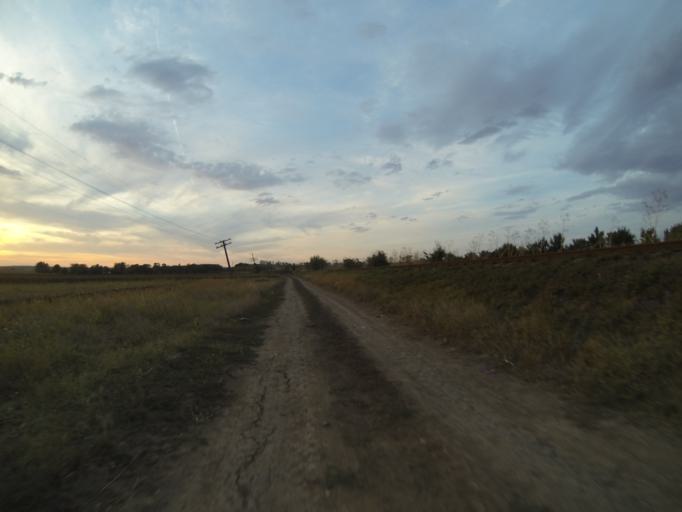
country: RO
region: Dolj
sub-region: Comuna Segarcea
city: Segarcea
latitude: 44.0984
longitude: 23.7244
